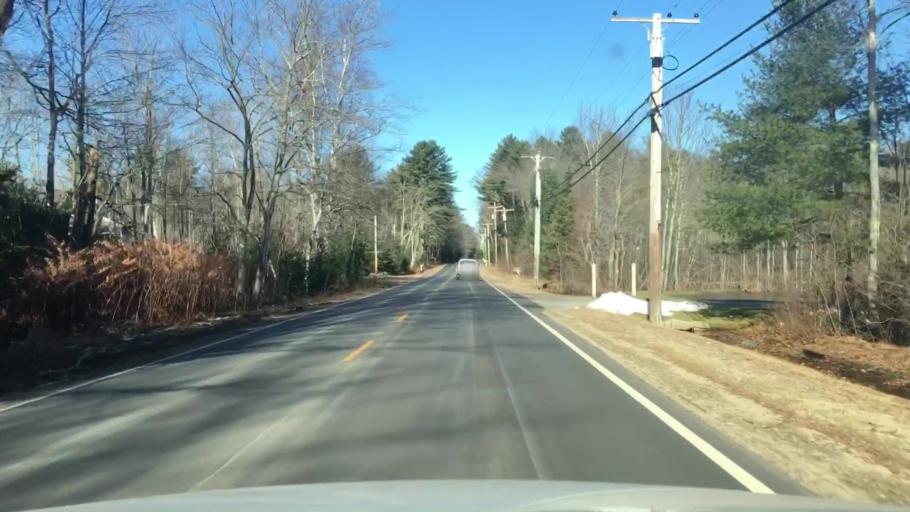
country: US
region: Maine
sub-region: York County
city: Arundel
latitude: 43.3883
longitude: -70.4806
